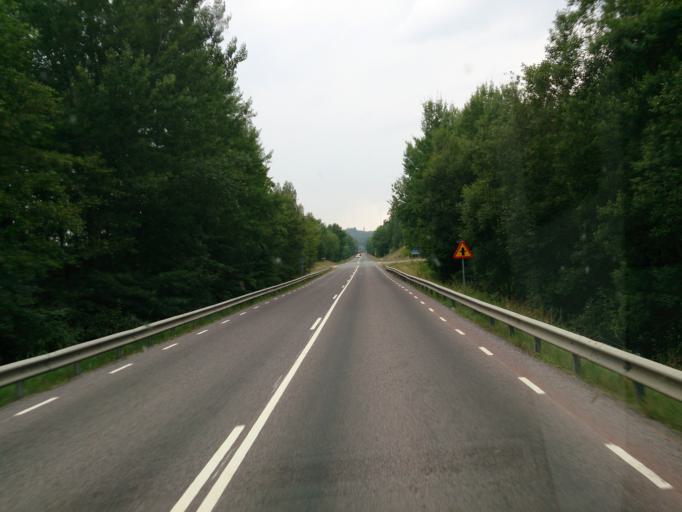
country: SE
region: Skane
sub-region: Kristianstads Kommun
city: Tollarp
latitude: 56.1760
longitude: 14.2913
